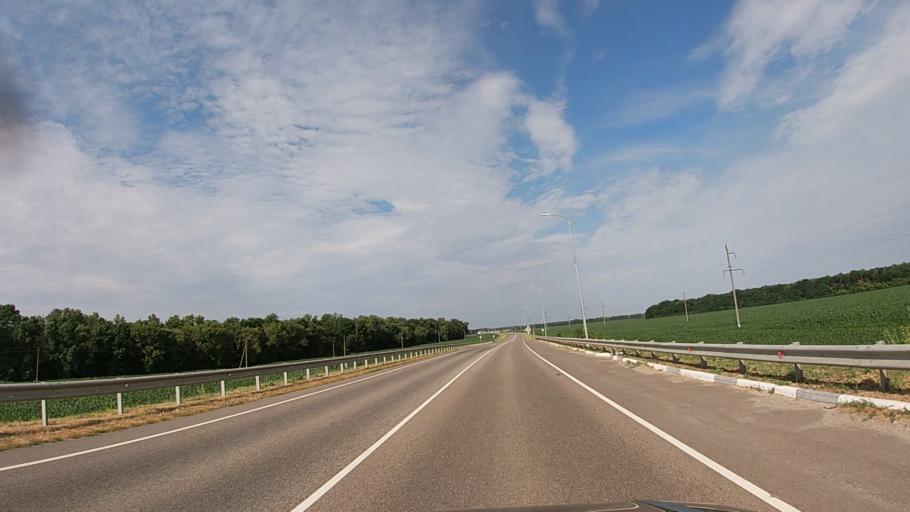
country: RU
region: Belgorod
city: Proletarskiy
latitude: 50.8018
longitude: 35.7347
